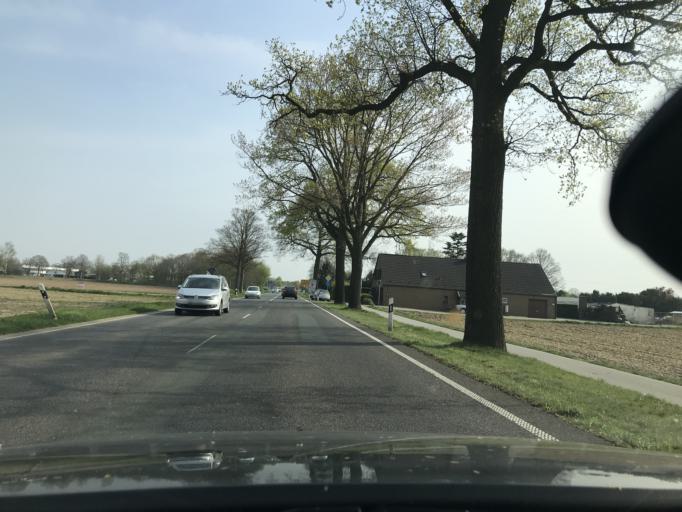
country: DE
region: North Rhine-Westphalia
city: Geldern
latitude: 51.5250
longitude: 6.2864
